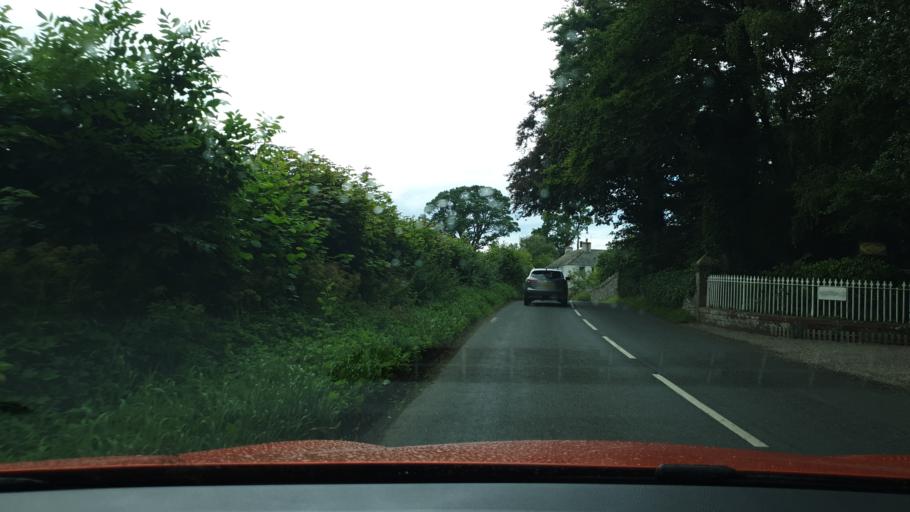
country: GB
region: England
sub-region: Cumbria
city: Penrith
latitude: 54.6178
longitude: -2.8082
